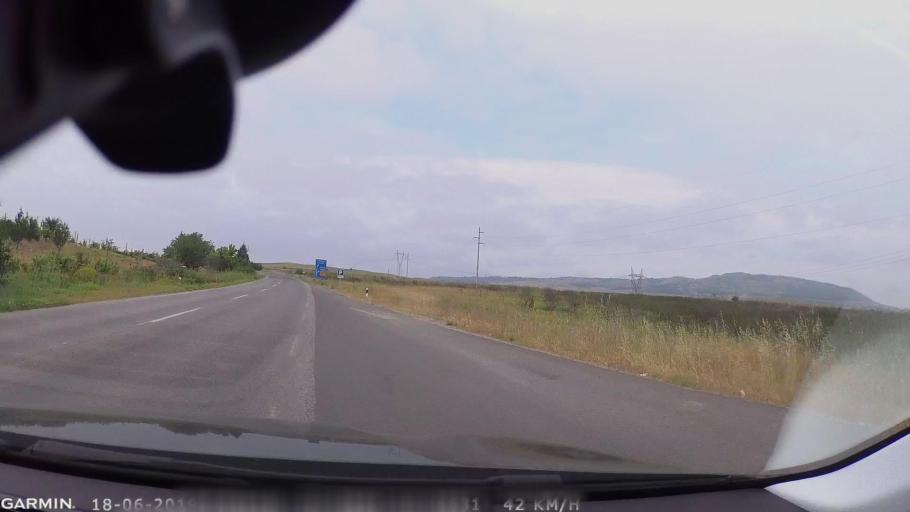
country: MK
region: Stip
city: Shtip
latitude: 41.7680
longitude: 22.1658
